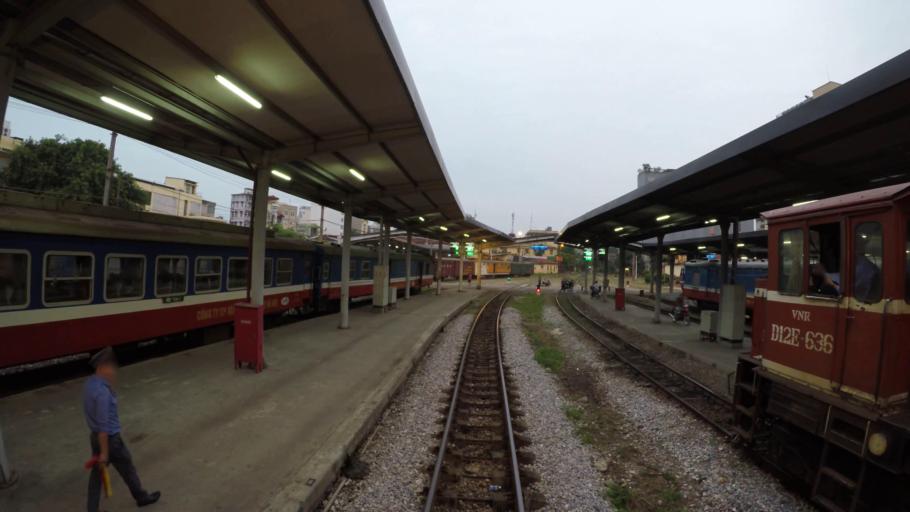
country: VN
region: Ha Noi
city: Hanoi
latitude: 21.0257
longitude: 105.8409
